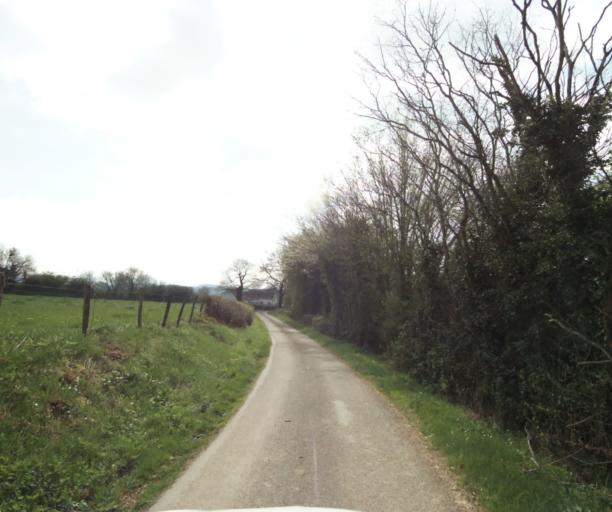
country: FR
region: Bourgogne
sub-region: Departement de Saone-et-Loire
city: Charolles
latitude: 46.3754
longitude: 4.3066
